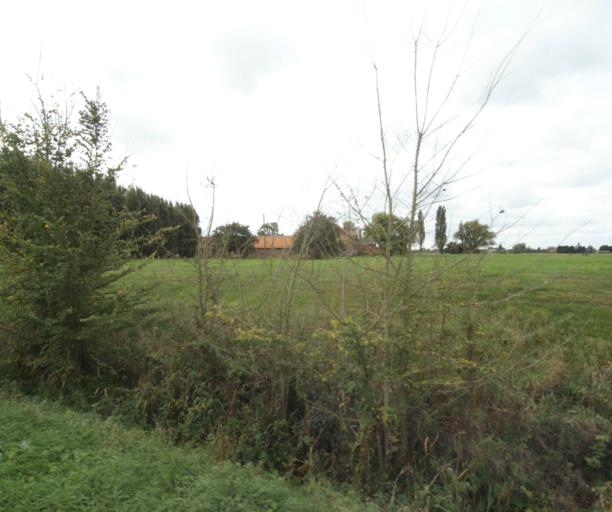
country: FR
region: Nord-Pas-de-Calais
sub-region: Departement du Nord
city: Erquinghem-Lys
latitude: 50.6702
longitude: 2.8552
